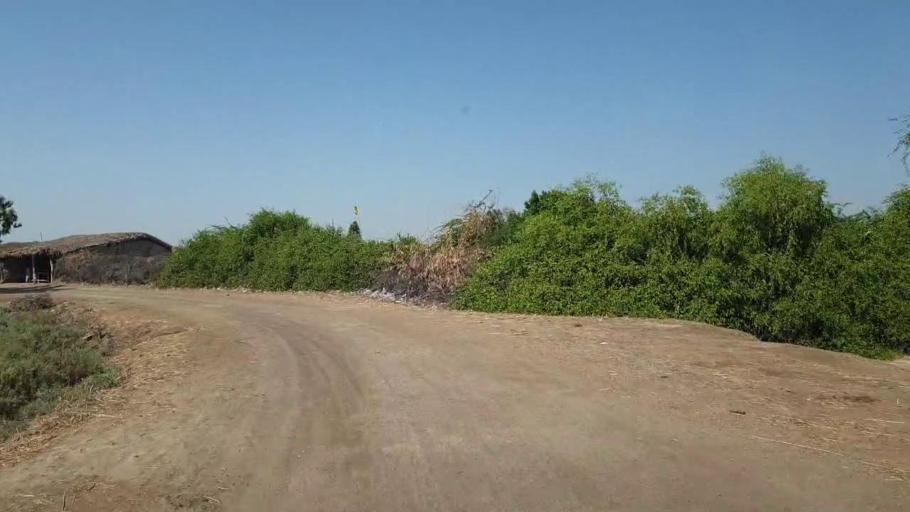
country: PK
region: Sindh
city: Tando Bago
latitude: 24.7062
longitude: 69.0158
